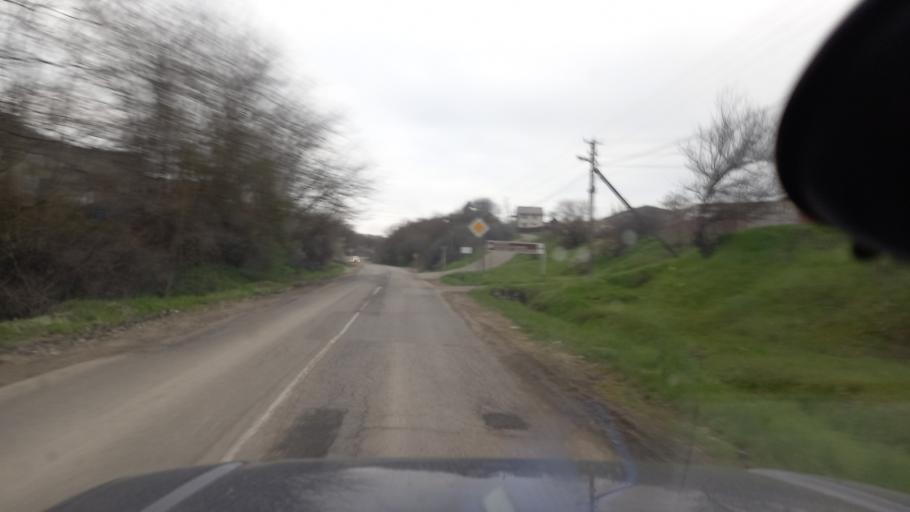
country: RU
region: Krasnodarskiy
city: Sukko
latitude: 44.8465
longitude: 37.4354
